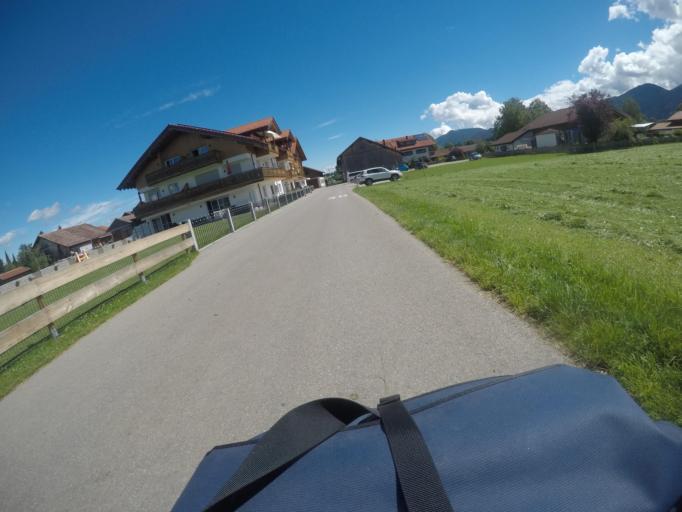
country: DE
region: Bavaria
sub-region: Swabia
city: Schwangau
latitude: 47.5927
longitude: 10.7391
